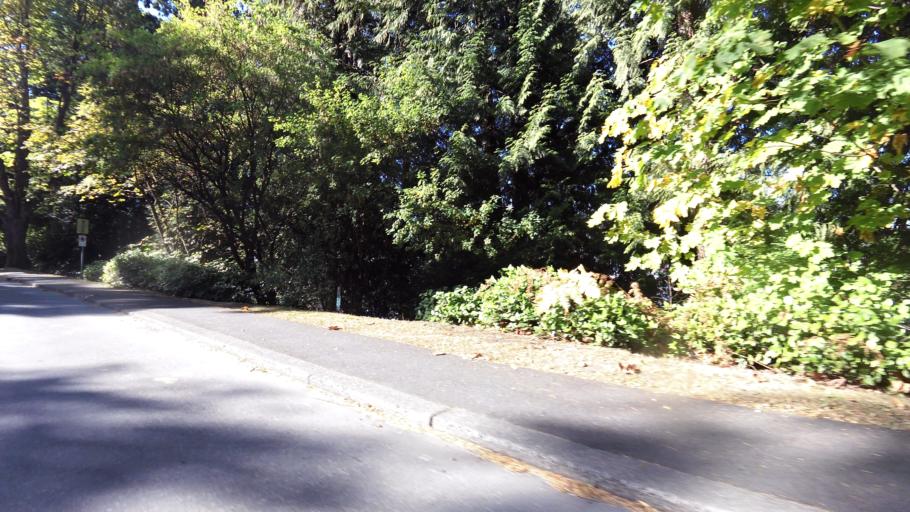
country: CA
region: British Columbia
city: West End
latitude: 49.2971
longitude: -123.1293
